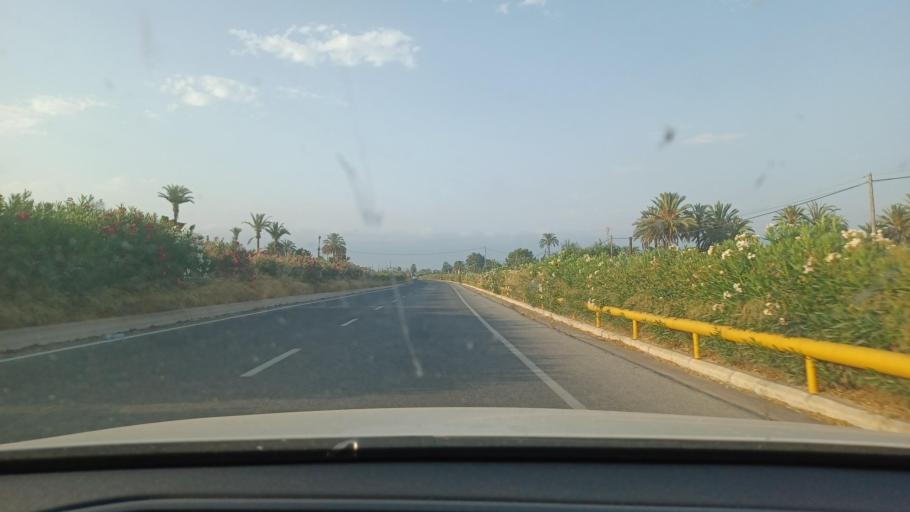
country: ES
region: Valencia
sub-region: Provincia de Alicante
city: Elche
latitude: 38.2122
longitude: -0.6976
